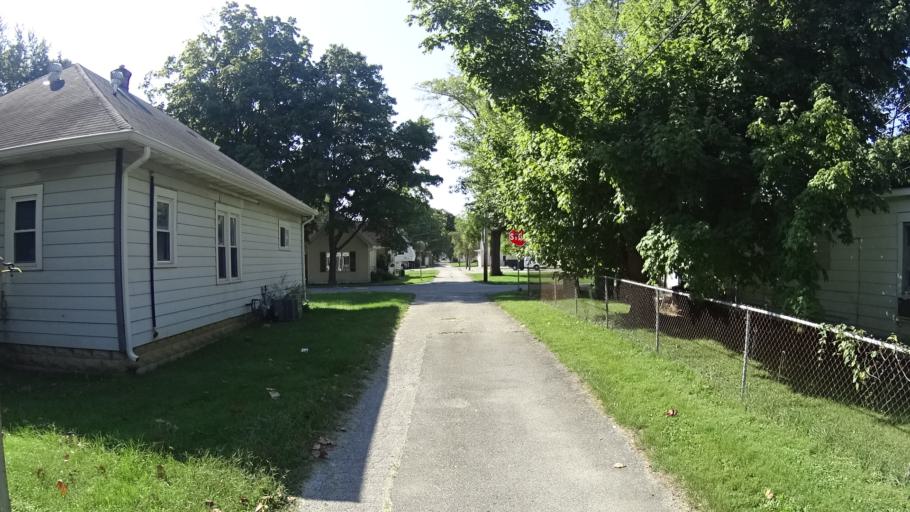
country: US
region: Indiana
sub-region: Madison County
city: Lapel
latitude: 40.0704
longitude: -85.8512
